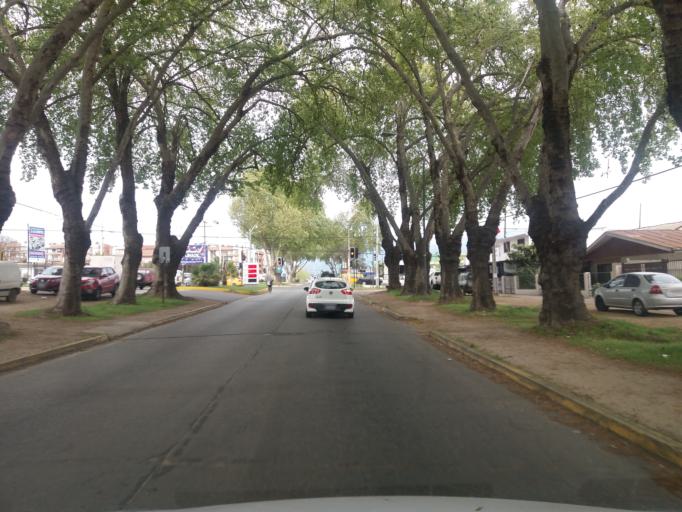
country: CL
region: Valparaiso
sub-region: Provincia de Marga Marga
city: Limache
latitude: -32.9903
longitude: -71.2645
